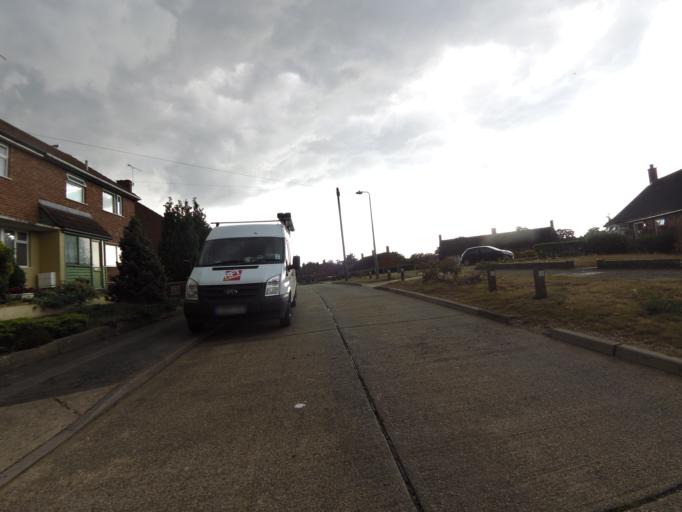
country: GB
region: England
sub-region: Suffolk
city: Ipswich
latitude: 52.0486
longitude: 1.1304
